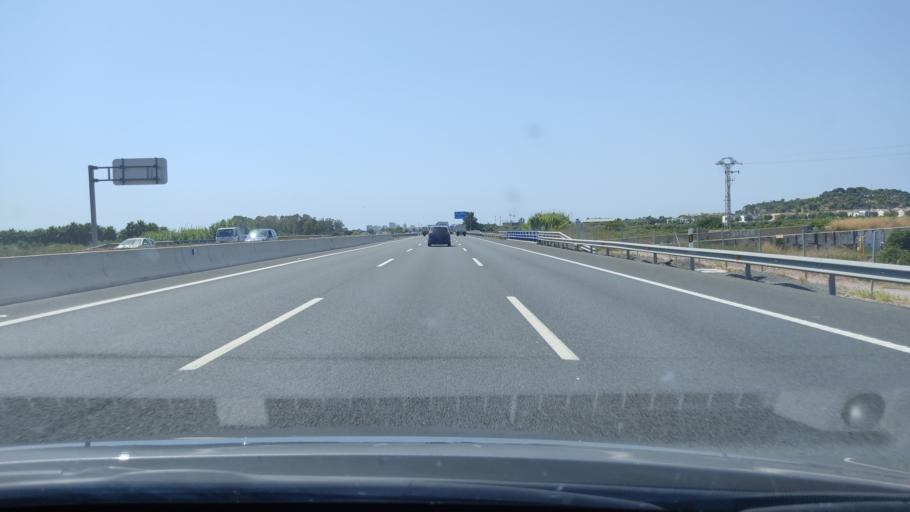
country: ES
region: Valencia
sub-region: Provincia de Valencia
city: Puig
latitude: 39.6013
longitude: -0.2938
